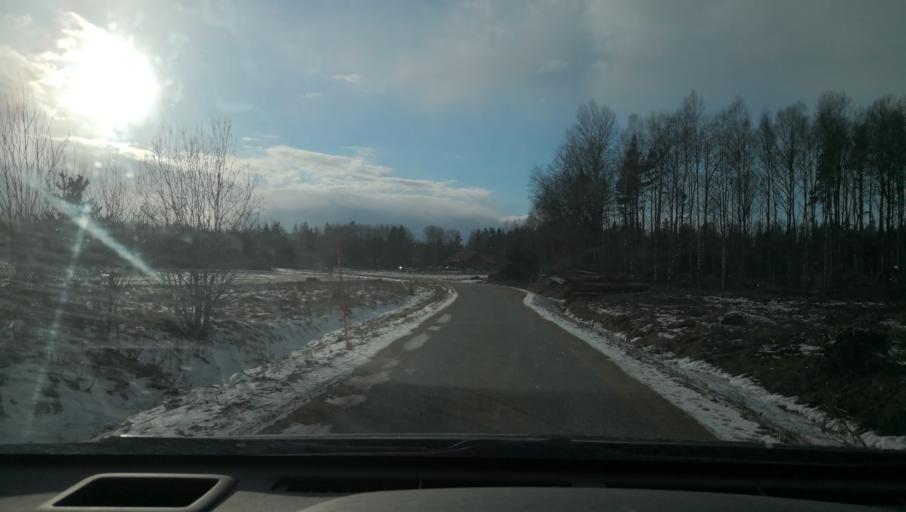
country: SE
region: Uppsala
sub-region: Enkopings Kommun
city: Irsta
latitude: 59.7086
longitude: 16.8977
